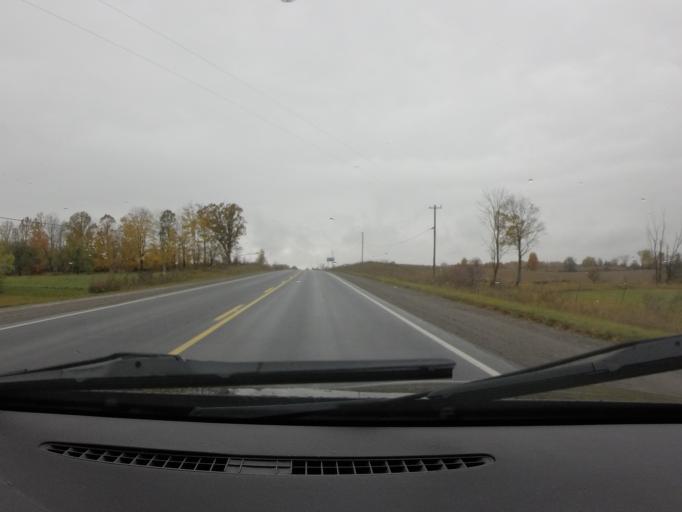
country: CA
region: Ontario
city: Belleville
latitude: 44.5201
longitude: -77.4378
